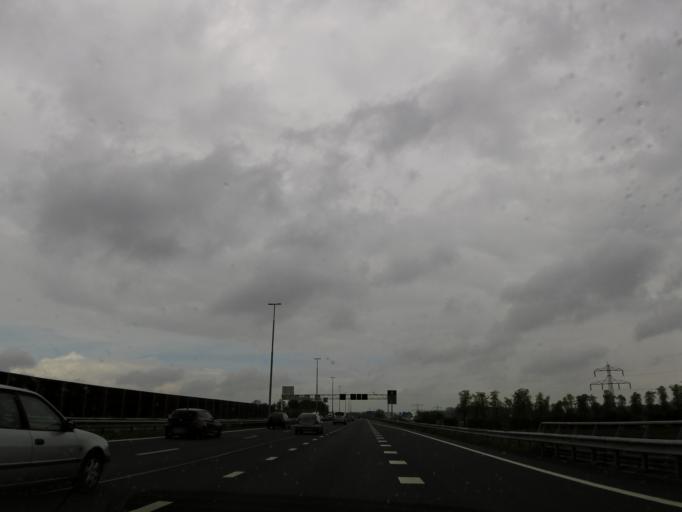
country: NL
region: Limburg
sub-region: Gemeente Sittard-Geleen
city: Born
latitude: 51.0443
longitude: 5.8263
